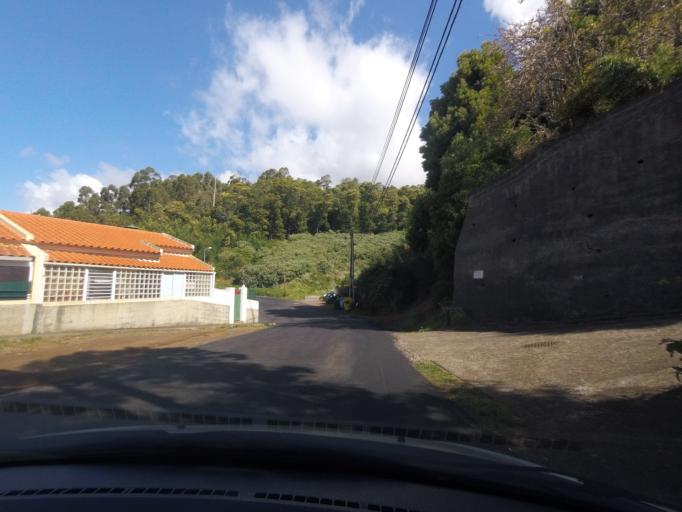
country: PT
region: Madeira
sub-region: Santa Cruz
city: Camacha
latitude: 32.6582
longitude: -16.8553
